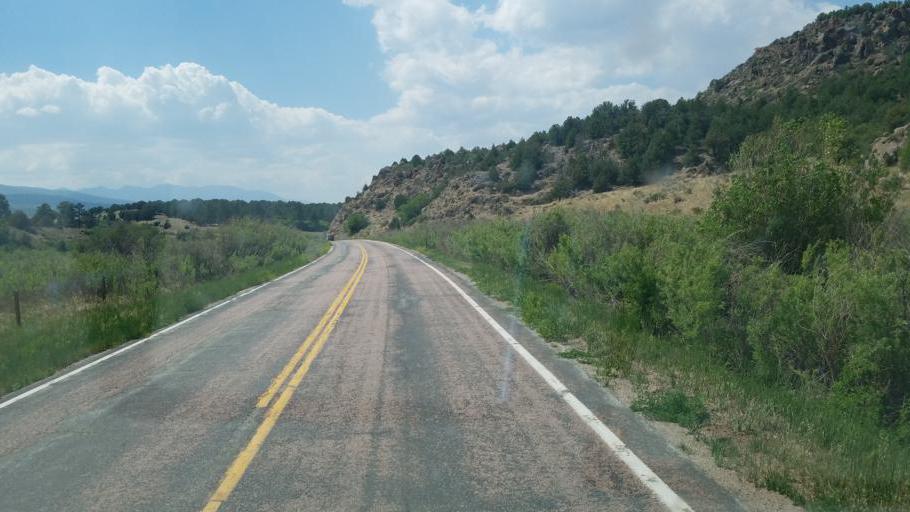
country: US
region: Colorado
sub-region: Custer County
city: Westcliffe
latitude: 38.2622
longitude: -105.5982
